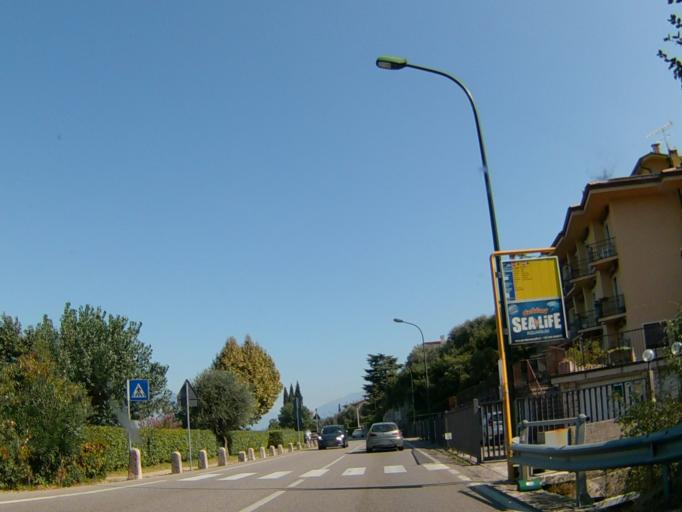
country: IT
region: Veneto
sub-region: Provincia di Verona
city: Brenzone
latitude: 45.6732
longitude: 10.7374
